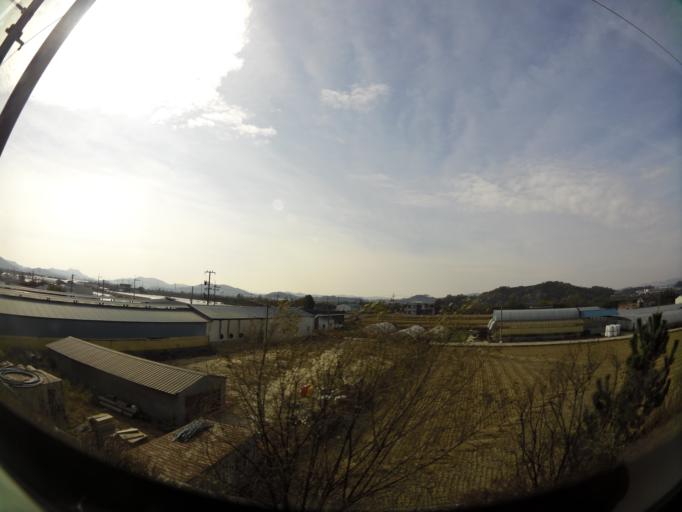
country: KR
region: Daejeon
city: Songgang-dong
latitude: 36.5771
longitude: 127.3108
